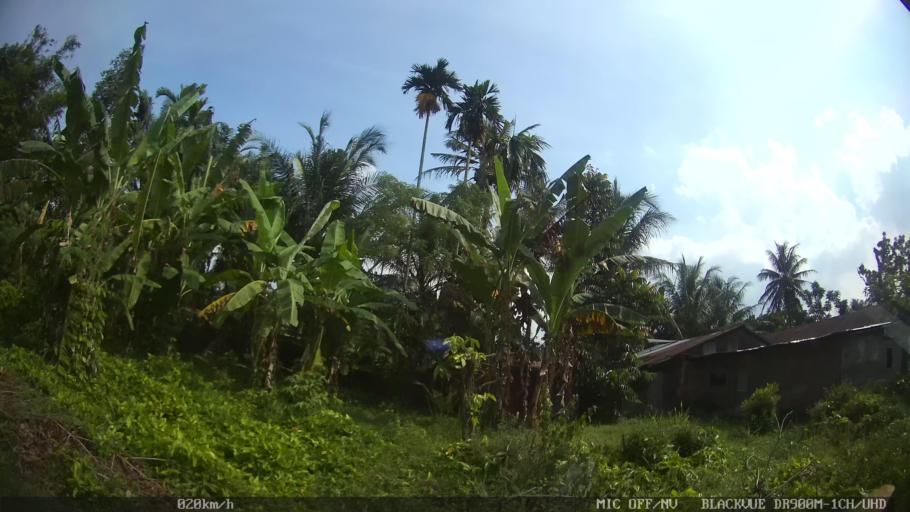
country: ID
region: North Sumatra
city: Binjai
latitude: 3.6426
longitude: 98.5182
